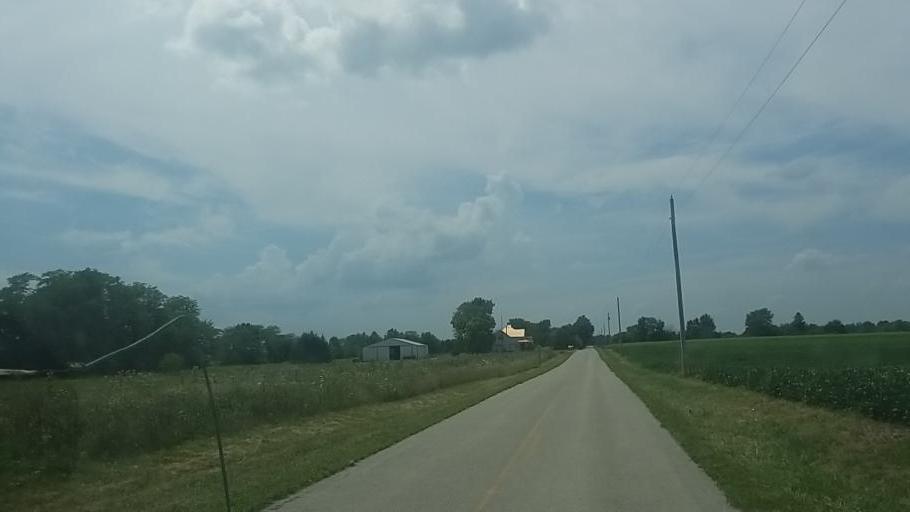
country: US
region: Ohio
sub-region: Hardin County
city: Kenton
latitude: 40.7393
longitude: -83.5922
